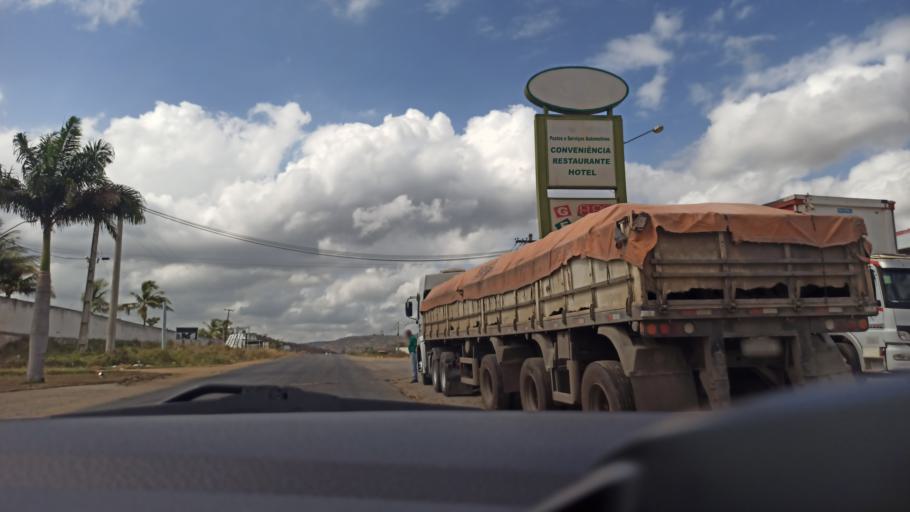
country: BR
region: Pernambuco
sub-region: Timbauba
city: Timbauba
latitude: -7.4954
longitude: -35.2975
